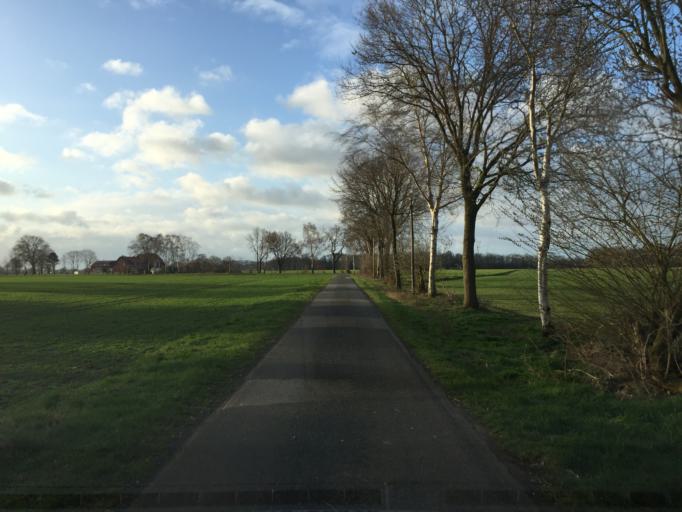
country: DE
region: Lower Saxony
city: Borstel
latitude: 52.6173
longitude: 8.9301
